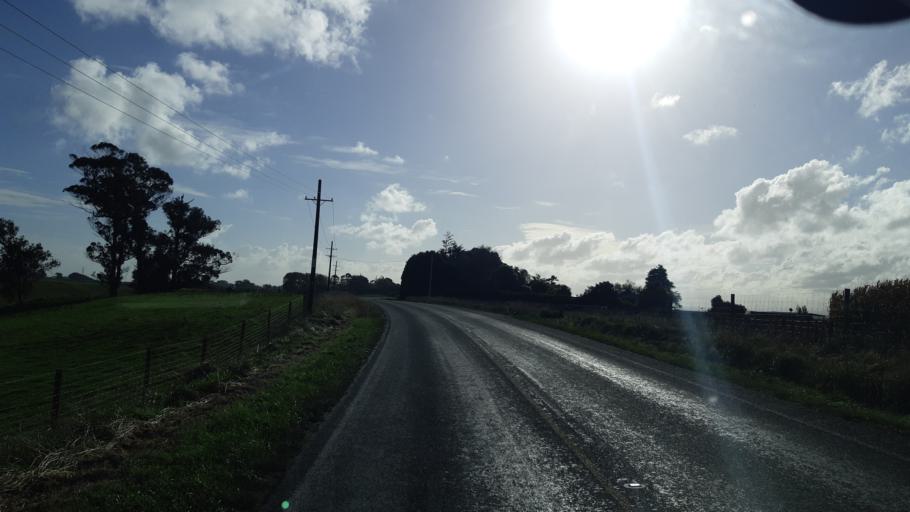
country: NZ
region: Manawatu-Wanganui
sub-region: Wanganui District
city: Wanganui
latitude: -39.9553
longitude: 175.1699
